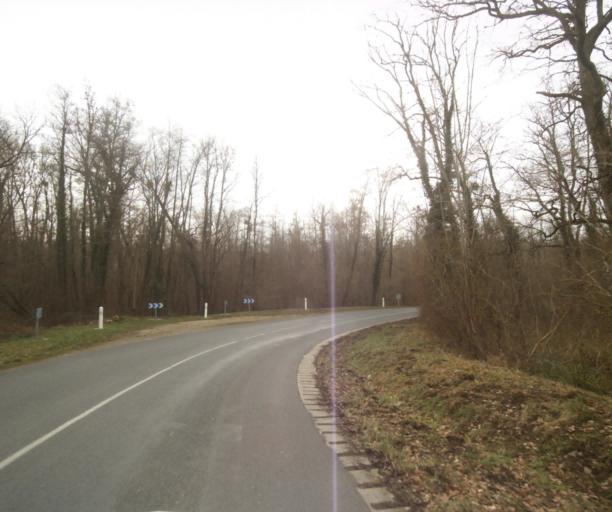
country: FR
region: Champagne-Ardenne
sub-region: Departement de la Haute-Marne
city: Villiers-en-Lieu
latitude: 48.6981
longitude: 4.8965
